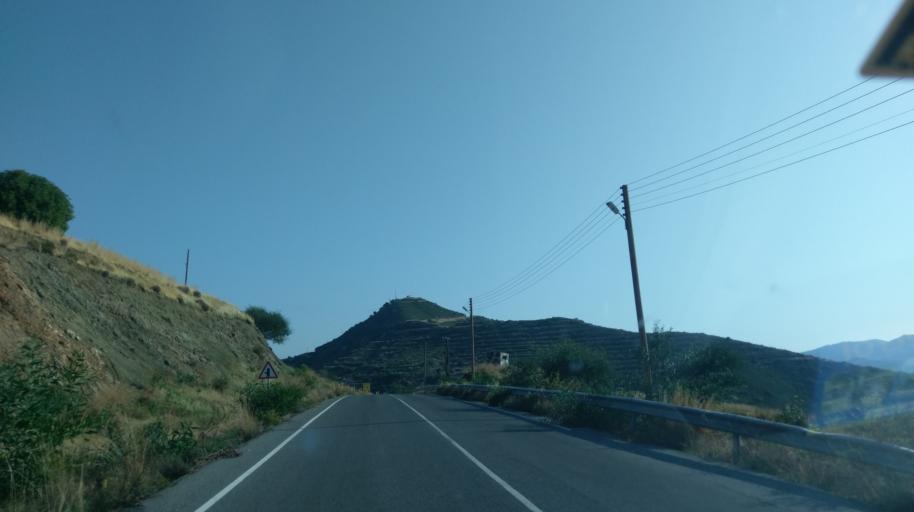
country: CY
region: Lefkosia
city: Kato Pyrgos
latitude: 35.1689
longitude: 32.7083
